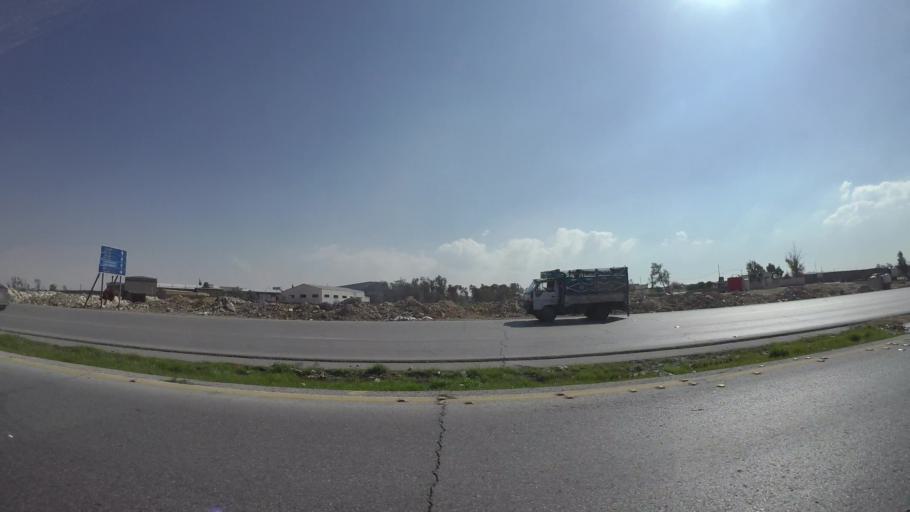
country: JO
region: Zarqa
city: Zarqa
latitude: 32.0274
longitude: 36.0929
